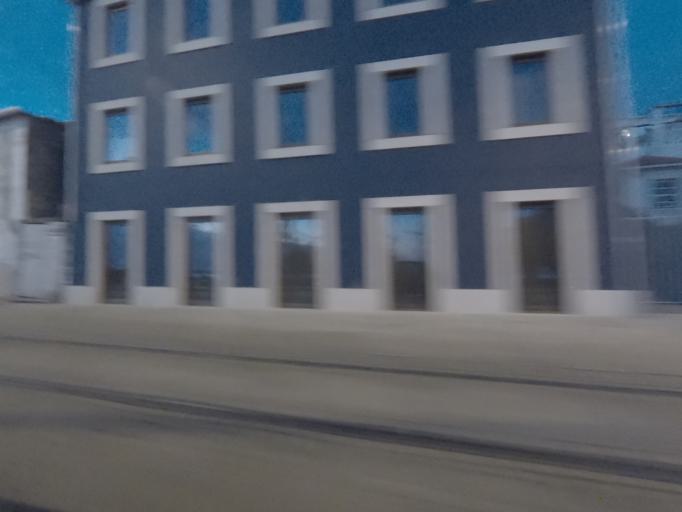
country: PT
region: Porto
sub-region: Vila Nova de Gaia
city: Canidelo
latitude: 41.1480
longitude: -8.6633
